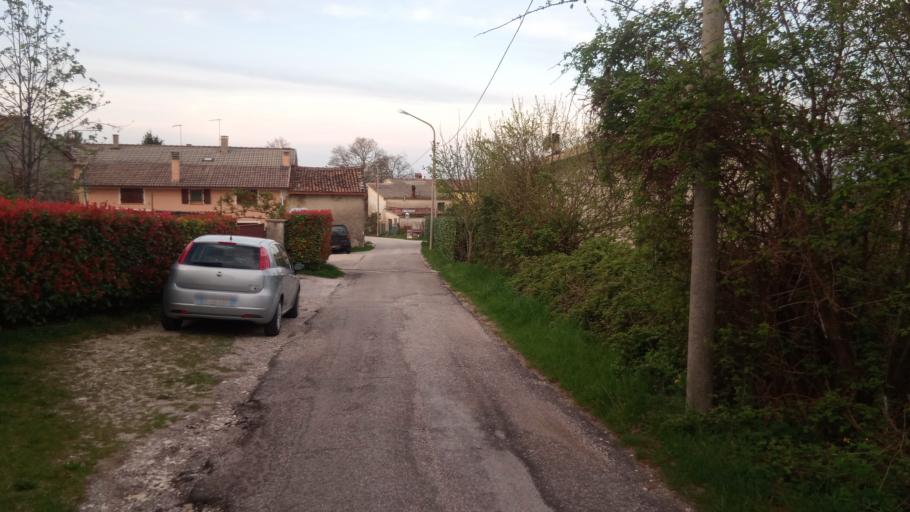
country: IT
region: Veneto
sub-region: Provincia di Vicenza
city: Conco
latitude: 45.7988
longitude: 11.6249
